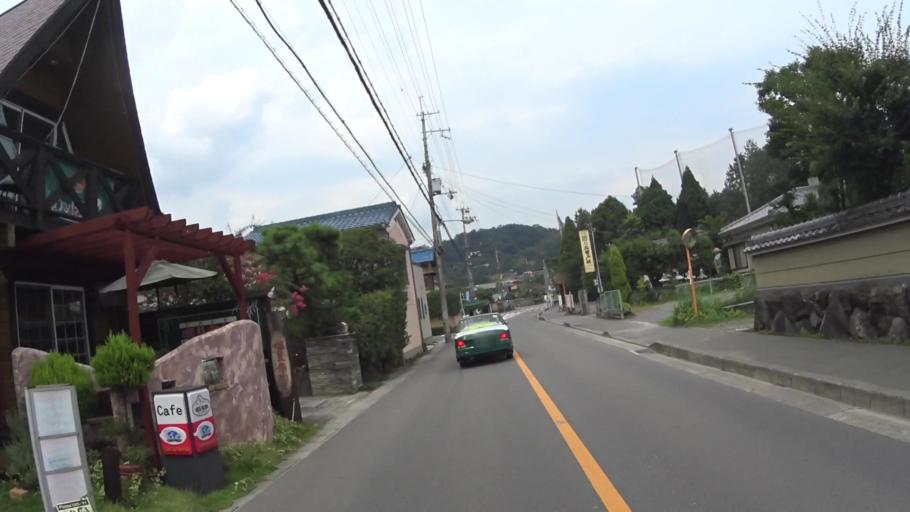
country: JP
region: Kyoto
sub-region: Kyoto-shi
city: Kamigyo-ku
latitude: 35.0681
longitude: 135.7520
